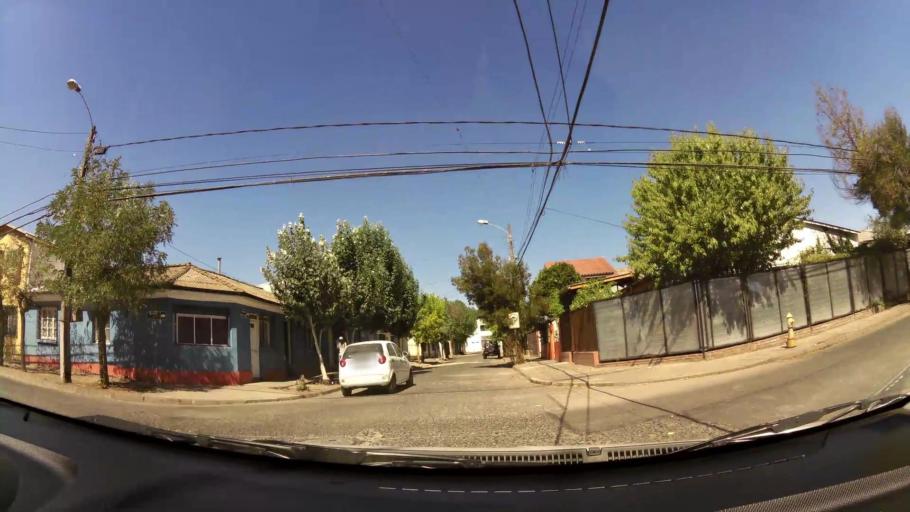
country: CL
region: O'Higgins
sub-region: Provincia de Colchagua
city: Chimbarongo
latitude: -34.5788
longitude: -70.9912
